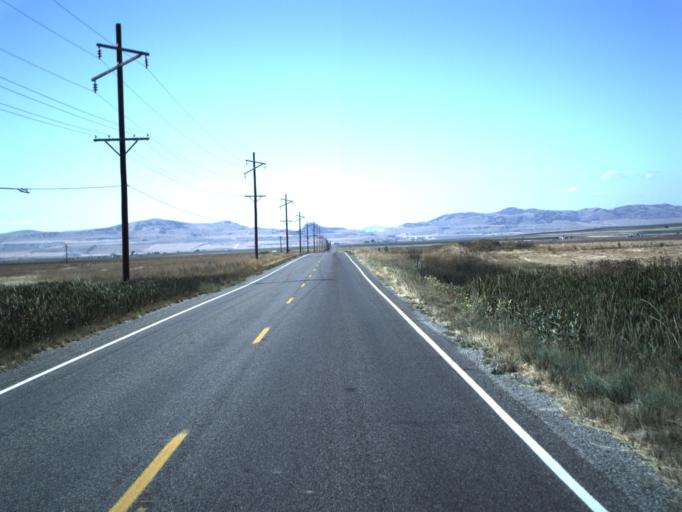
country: US
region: Utah
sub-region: Cache County
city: Benson
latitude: 41.8451
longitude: -111.9185
